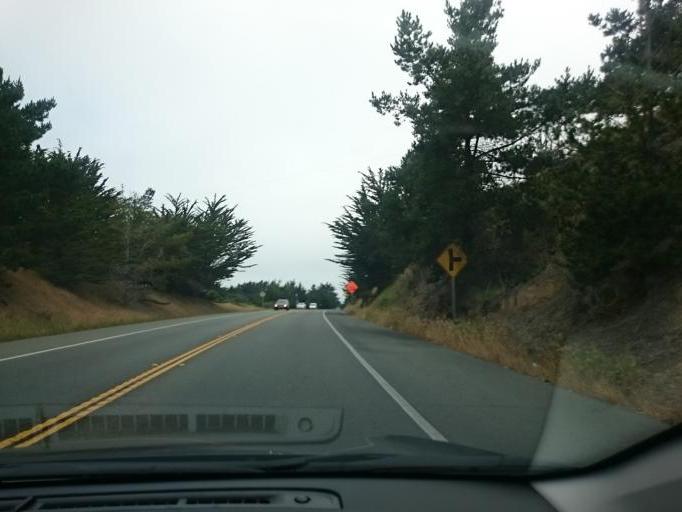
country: US
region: California
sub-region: San Mateo County
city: Moss Beach
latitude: 37.5336
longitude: -122.5178
